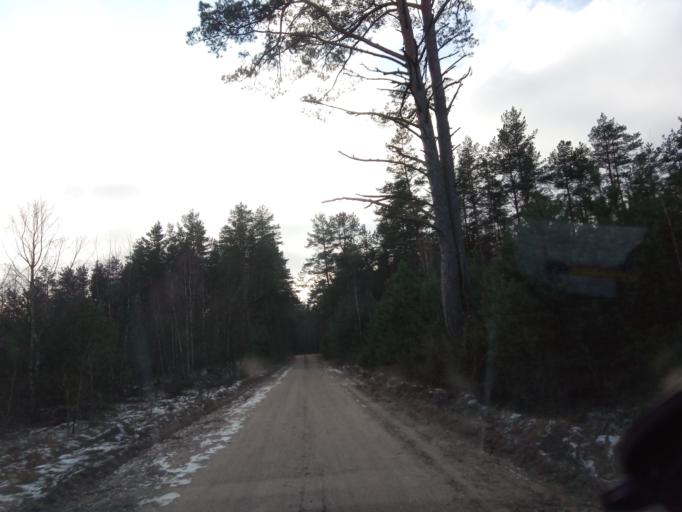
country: LT
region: Alytaus apskritis
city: Varena
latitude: 53.9818
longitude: 24.3342
